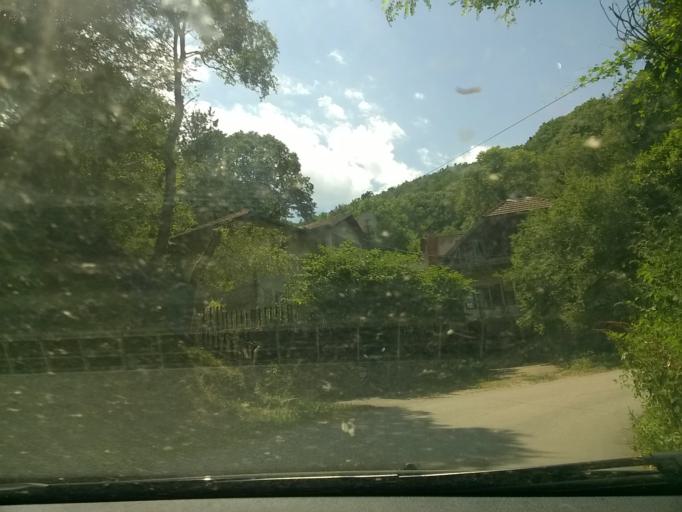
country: RS
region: Central Serbia
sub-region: Zajecarski Okrug
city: Soko Banja
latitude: 43.6333
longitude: 21.8683
